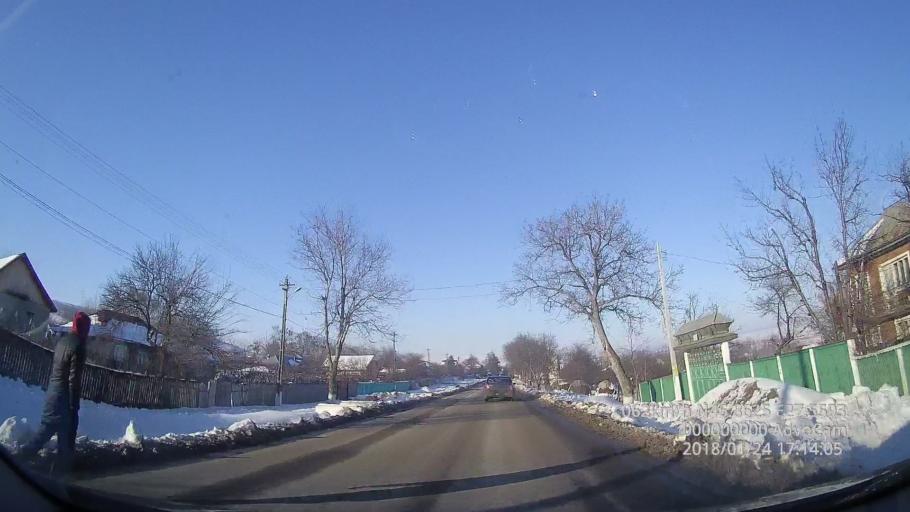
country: RO
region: Vaslui
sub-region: Comuna Rebricea
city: Rebricea
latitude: 46.8630
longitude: 27.5592
